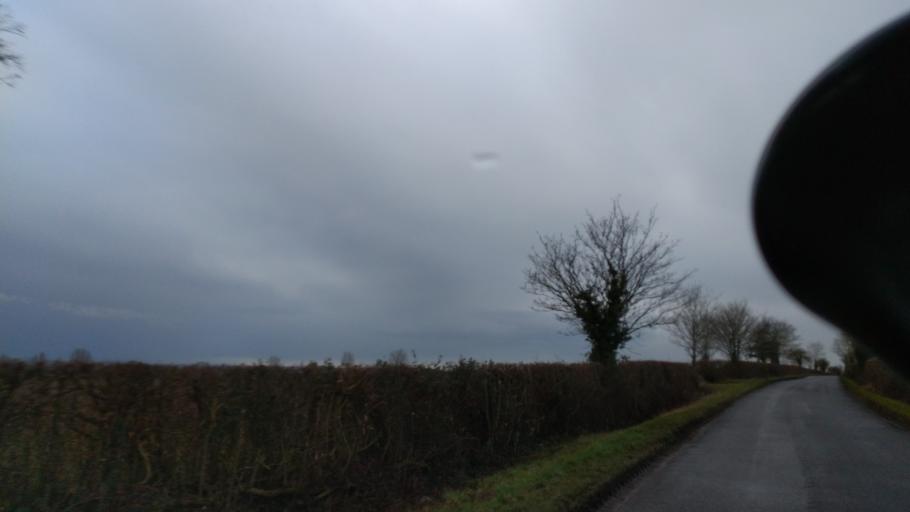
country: GB
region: England
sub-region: Borough of Swindon
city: Highworth
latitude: 51.6089
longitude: -1.7162
